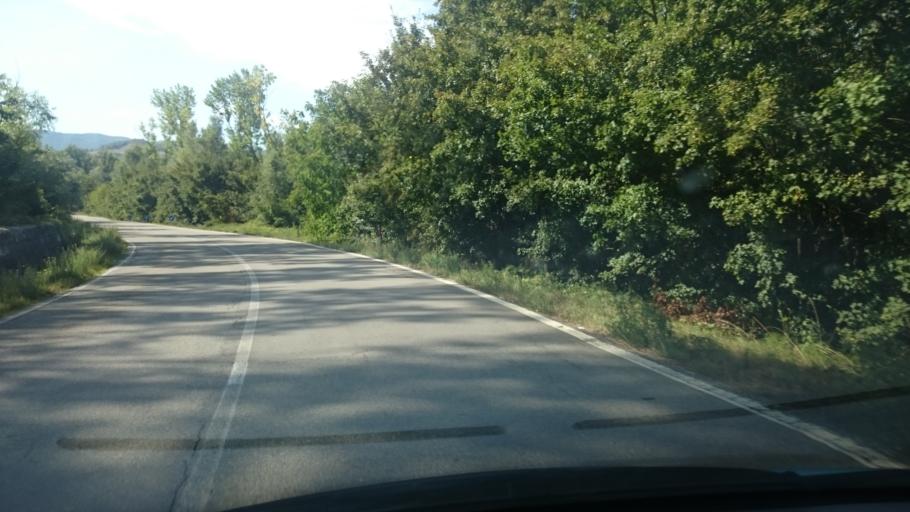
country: IT
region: Emilia-Romagna
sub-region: Provincia di Reggio Emilia
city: Toano
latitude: 44.4150
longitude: 10.5813
